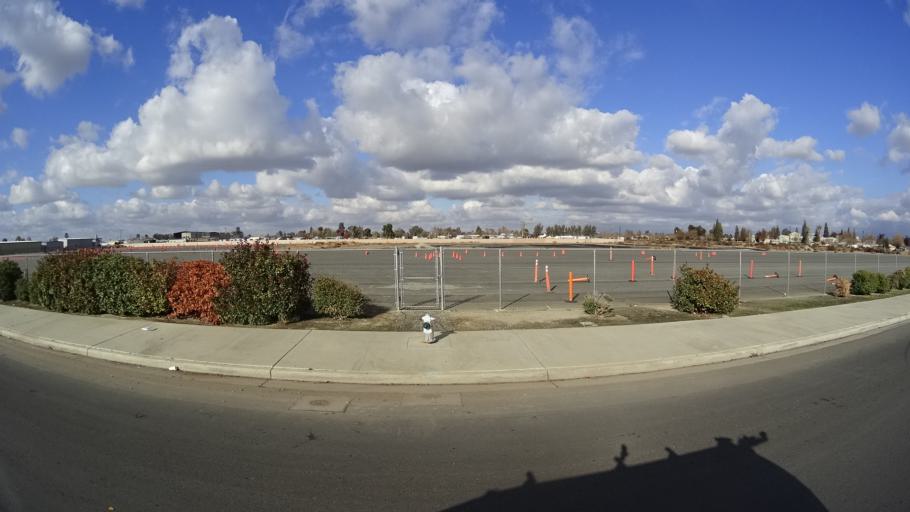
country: US
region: California
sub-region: Kern County
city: Bakersfield
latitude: 35.3322
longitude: -118.9964
